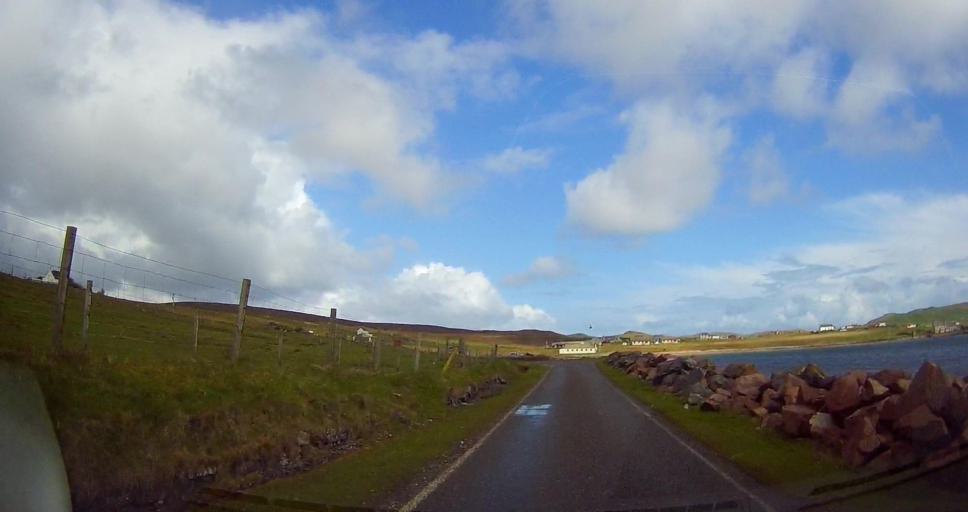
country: GB
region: Scotland
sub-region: Shetland Islands
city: Lerwick
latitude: 60.5815
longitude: -1.3342
